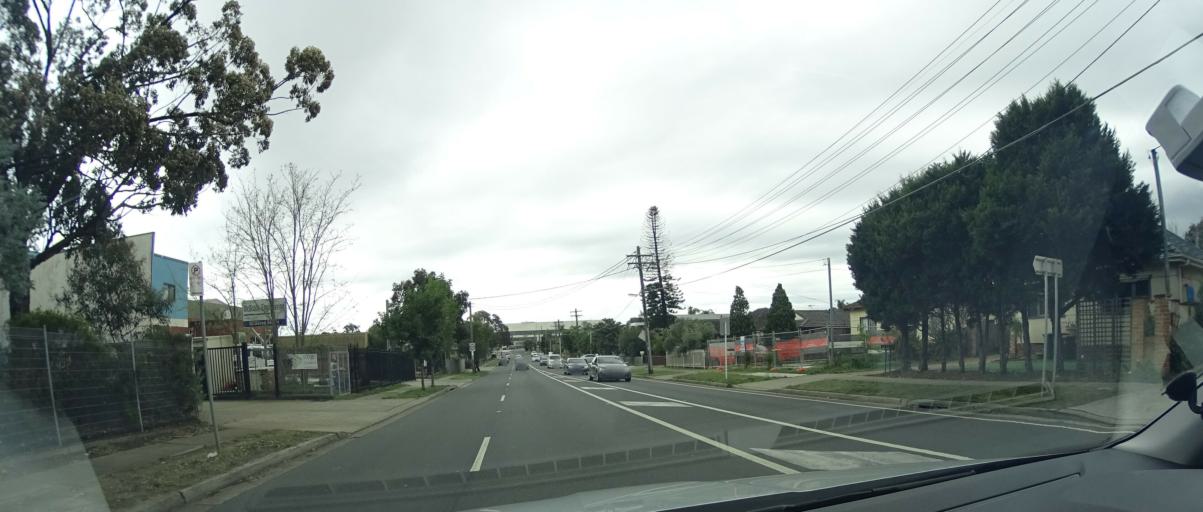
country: AU
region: New South Wales
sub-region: Bankstown
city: Revesby
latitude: -33.9388
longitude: 151.0112
